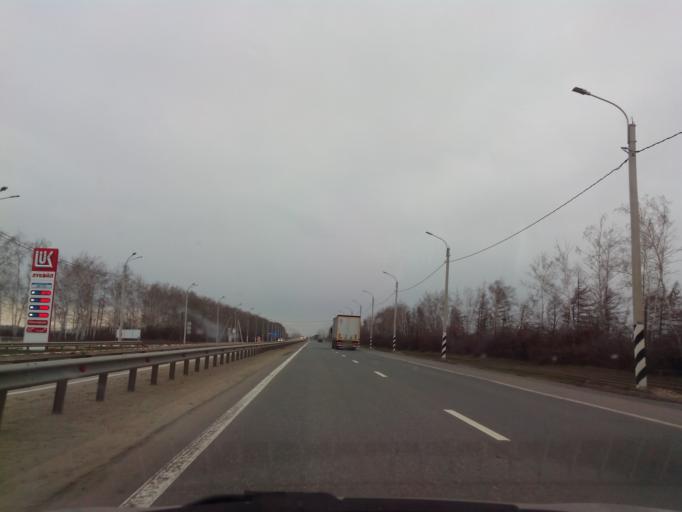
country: RU
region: Tambov
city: Komsomolets
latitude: 52.7355
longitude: 41.2749
